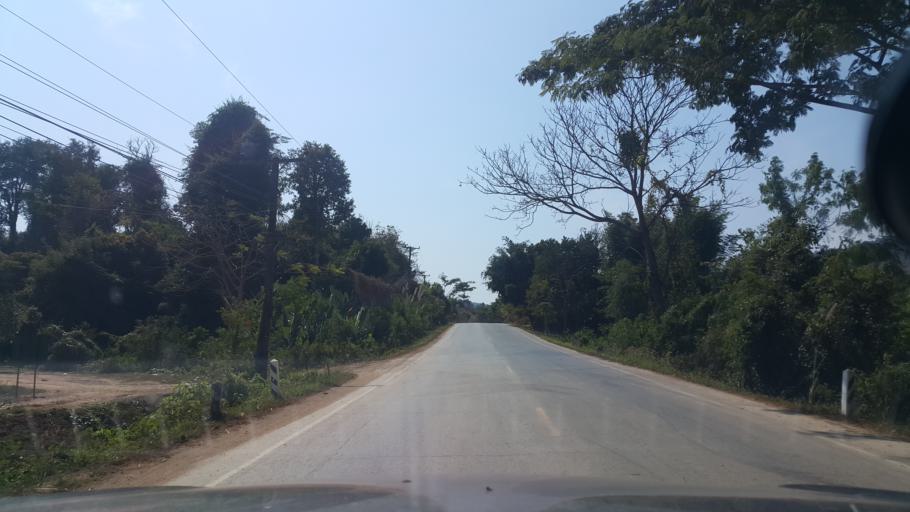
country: TH
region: Changwat Udon Thani
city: Na Yung
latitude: 17.9150
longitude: 102.0713
